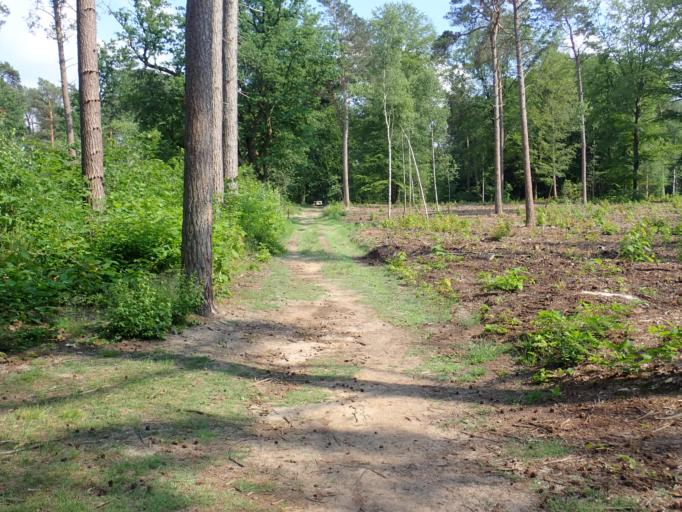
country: BE
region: Flanders
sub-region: Provincie Antwerpen
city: Kasterlee
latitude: 51.2306
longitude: 4.9535
